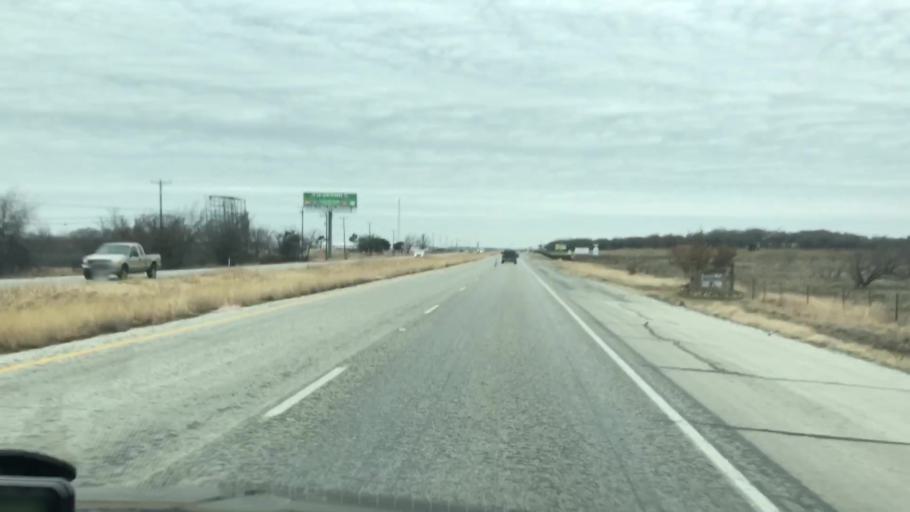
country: US
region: Texas
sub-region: Jack County
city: Jacksboro
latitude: 33.1921
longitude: -98.1387
